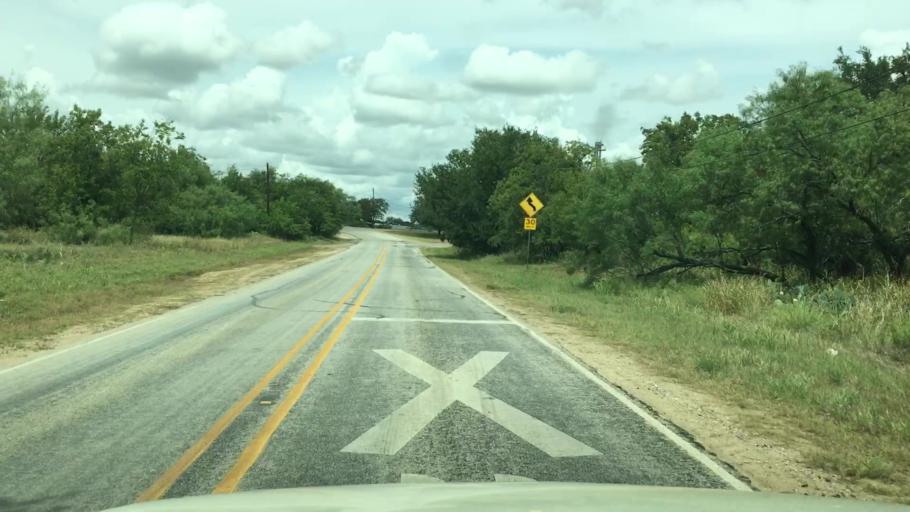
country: US
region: Texas
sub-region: McCulloch County
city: Brady
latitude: 31.1214
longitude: -99.3230
